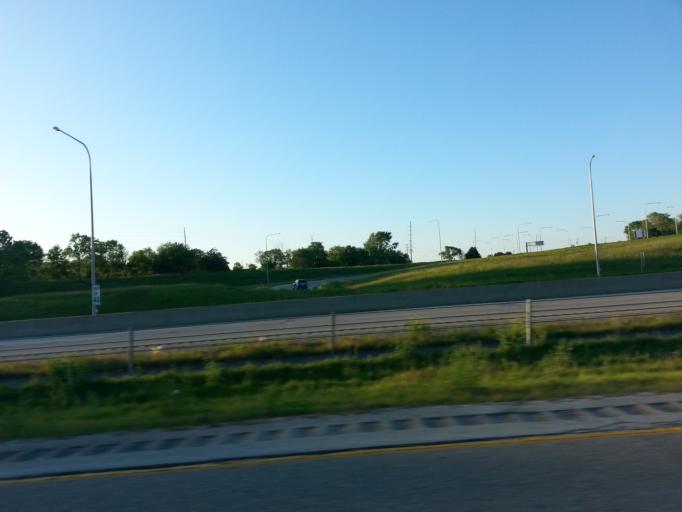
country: US
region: Illinois
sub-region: Vermilion County
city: Tilton
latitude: 40.1048
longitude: -87.6374
